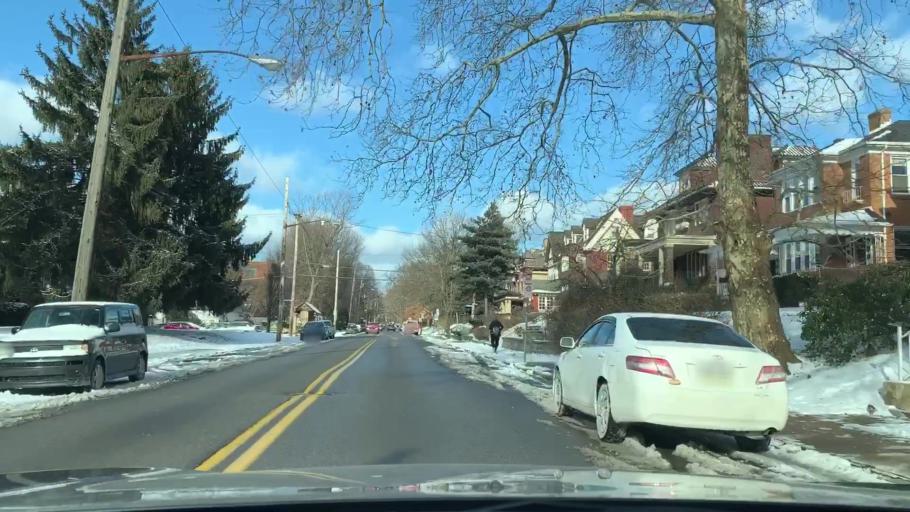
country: US
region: Pennsylvania
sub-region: Allegheny County
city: Sharpsburg
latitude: 40.4734
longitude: -79.9254
